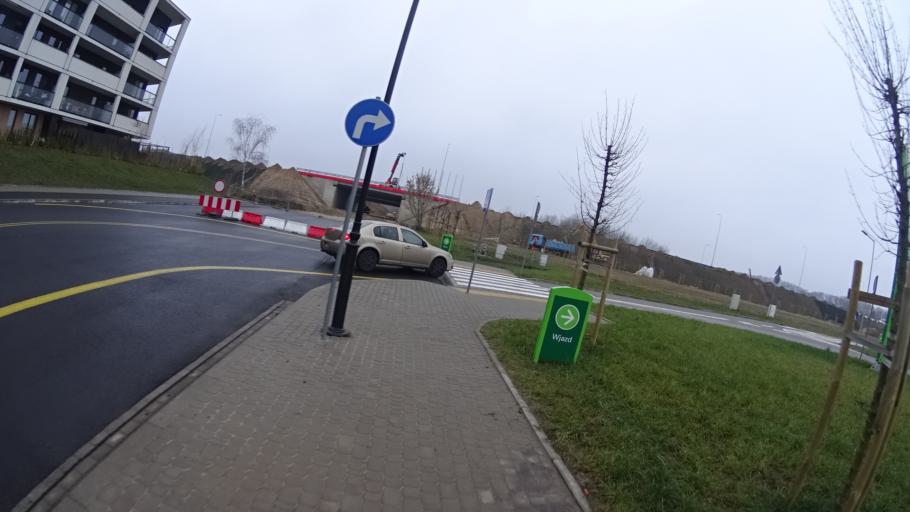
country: PL
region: Masovian Voivodeship
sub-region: Warszawa
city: Wilanow
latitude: 52.1541
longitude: 21.0711
